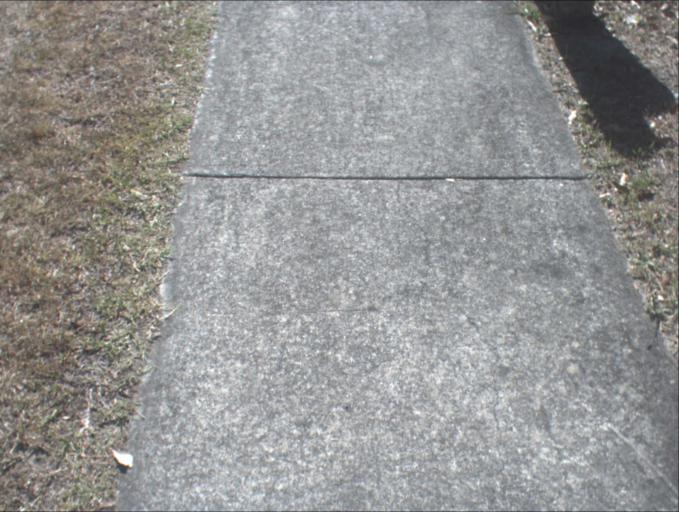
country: AU
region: Queensland
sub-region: Logan
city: Windaroo
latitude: -27.7254
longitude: 153.1846
